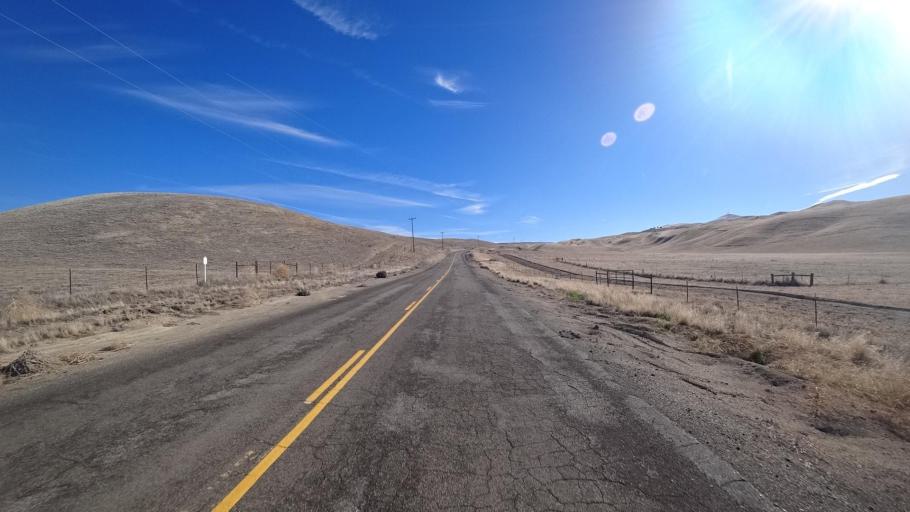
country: US
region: California
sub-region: Kern County
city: Maricopa
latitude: 34.9523
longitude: -119.4269
